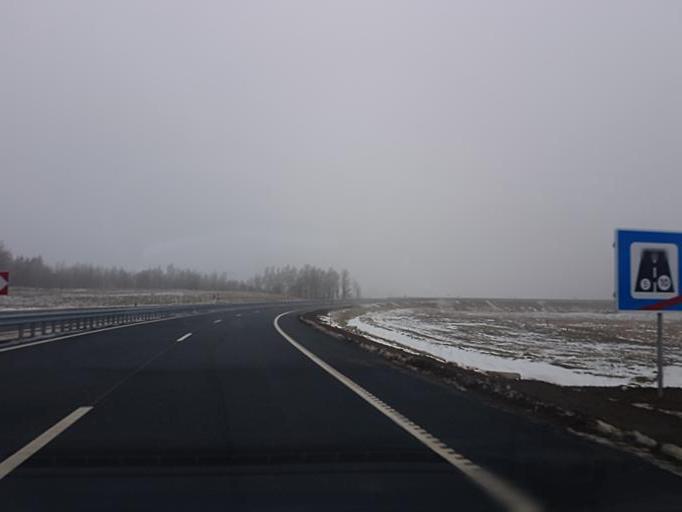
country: BY
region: Minsk
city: Samakhvalavichy
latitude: 53.7058
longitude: 27.4515
